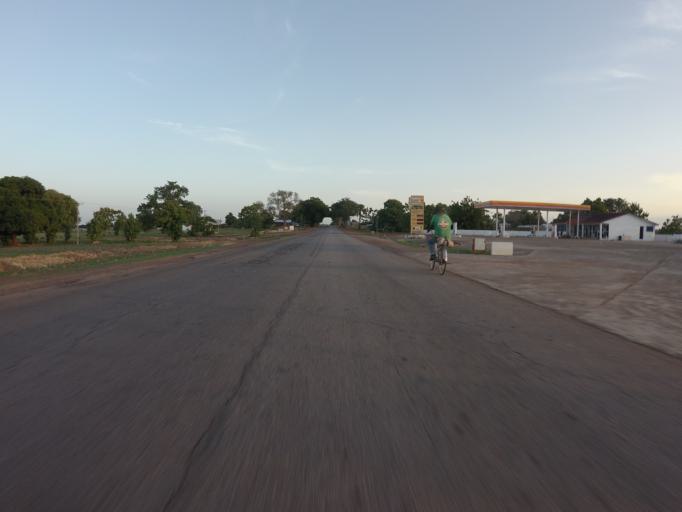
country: GH
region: Upper East
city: Navrongo
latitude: 10.9236
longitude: -1.0892
